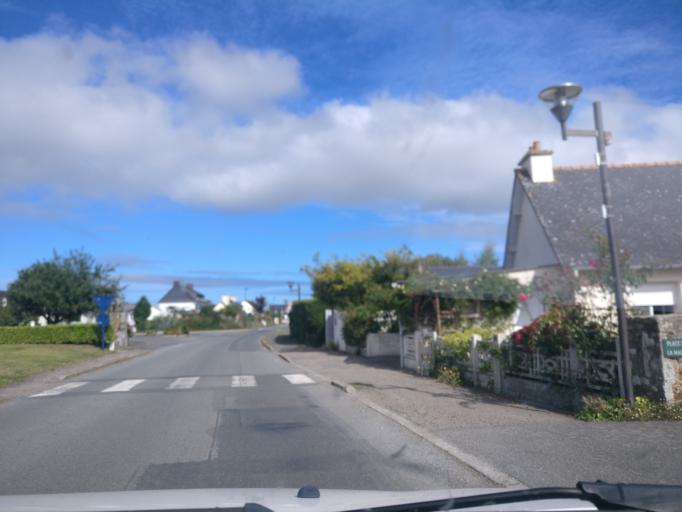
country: FR
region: Brittany
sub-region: Departement des Cotes-d'Armor
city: Rospez
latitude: 48.7580
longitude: -3.3672
